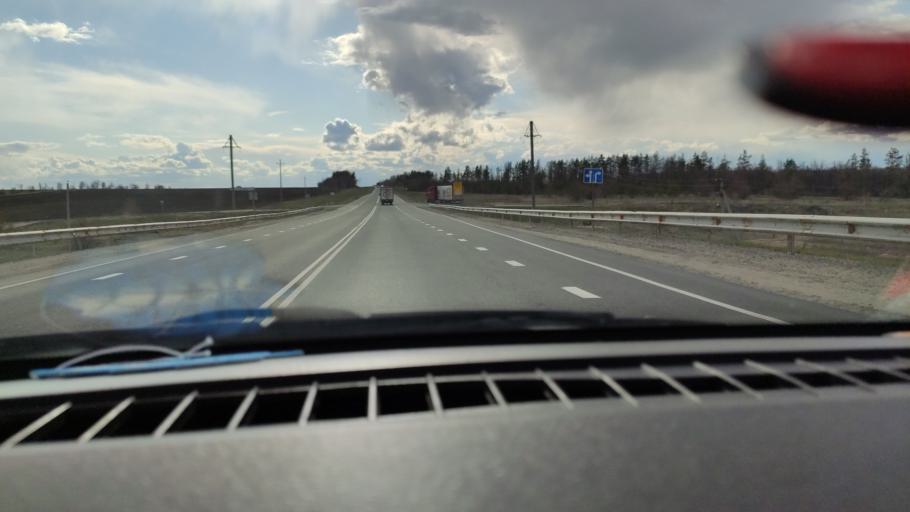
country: RU
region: Saratov
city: Sennoy
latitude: 52.1575
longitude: 47.0282
